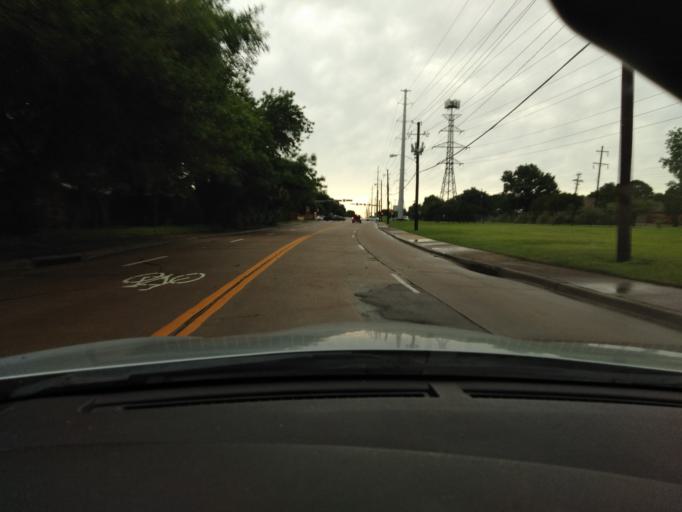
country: US
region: Texas
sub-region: Dallas County
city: Addison
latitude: 32.9767
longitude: -96.7787
